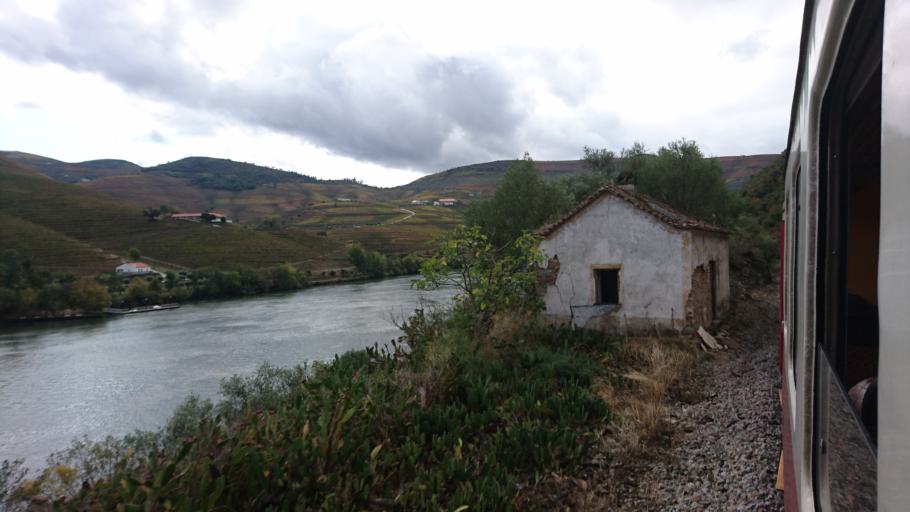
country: PT
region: Viseu
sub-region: Tabuaco
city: Tabuaco
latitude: 41.1908
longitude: -7.5161
